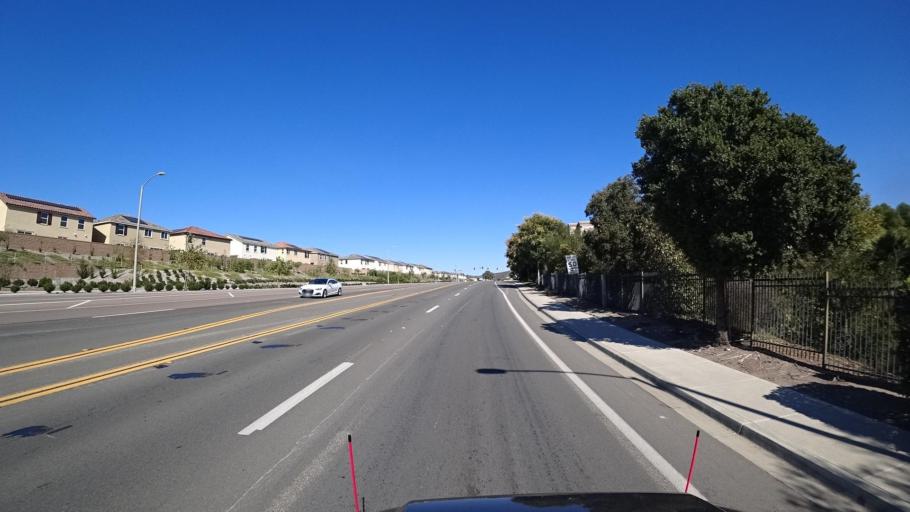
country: US
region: California
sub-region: San Diego County
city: La Presa
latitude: 32.7262
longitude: -116.9683
